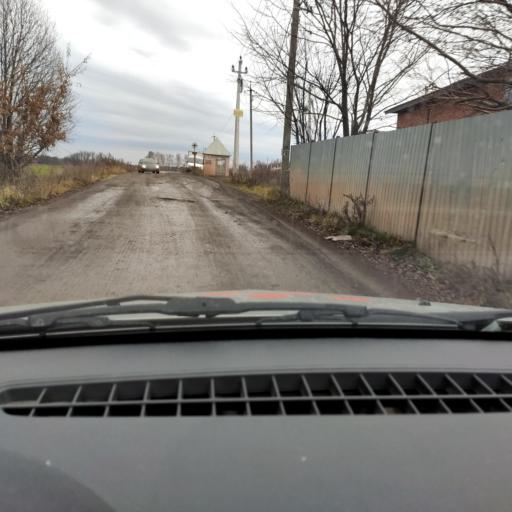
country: RU
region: Bashkortostan
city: Mikhaylovka
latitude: 54.8344
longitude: 55.9464
